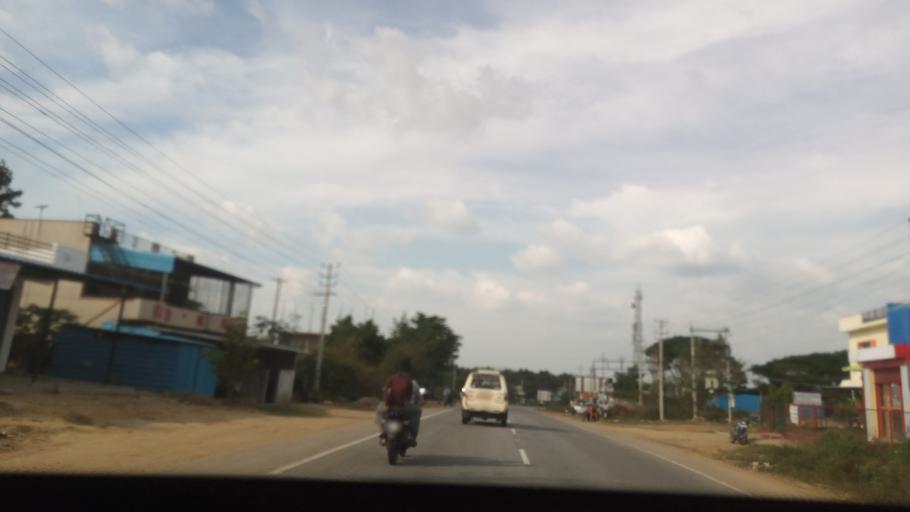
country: IN
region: Karnataka
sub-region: Mandya
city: Maddur
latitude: 12.6830
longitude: 77.0587
